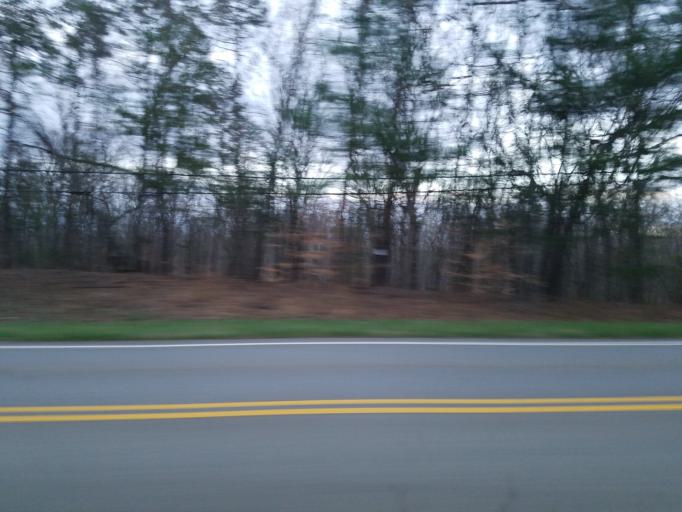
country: US
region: Georgia
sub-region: Pickens County
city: Nelson
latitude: 34.4071
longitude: -84.3857
